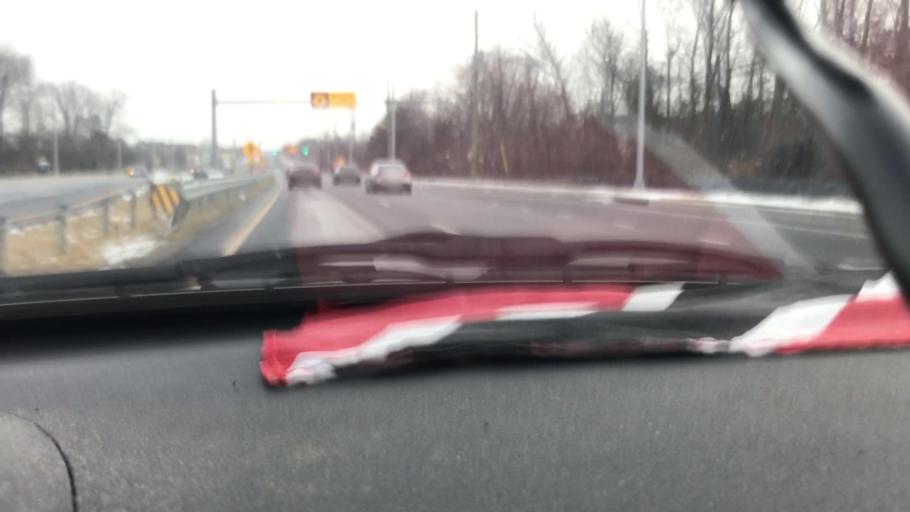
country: US
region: Maryland
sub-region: Prince George's County
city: District Heights
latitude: 38.8449
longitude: -76.8908
